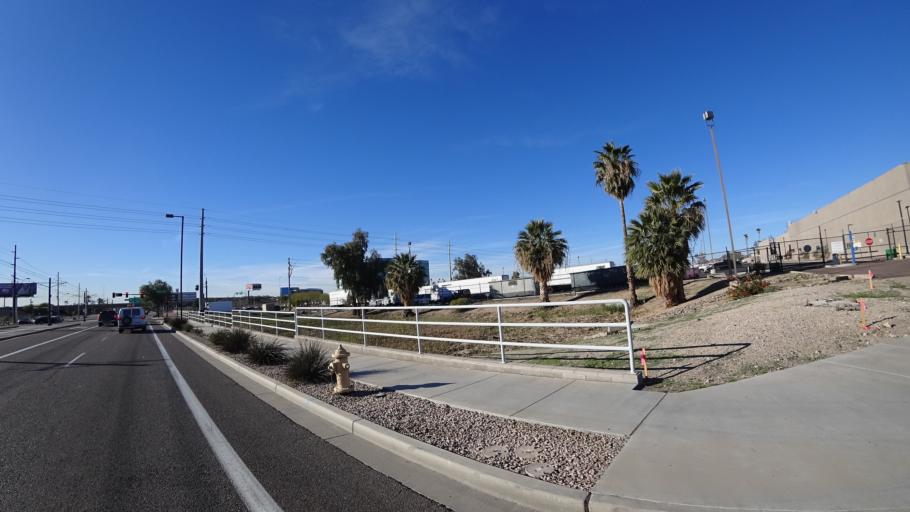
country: US
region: Arizona
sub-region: Maricopa County
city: Tempe Junction
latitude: 33.4474
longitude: -111.9776
